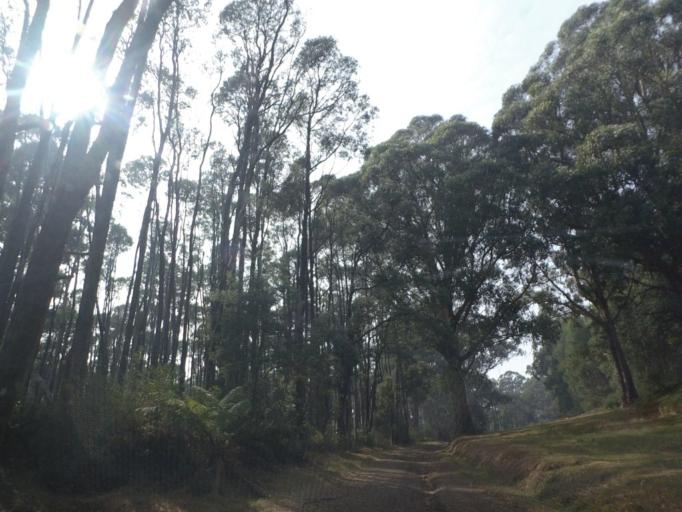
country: AU
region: Victoria
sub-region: Yarra Ranges
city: Healesville
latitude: -37.5652
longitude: 145.5901
